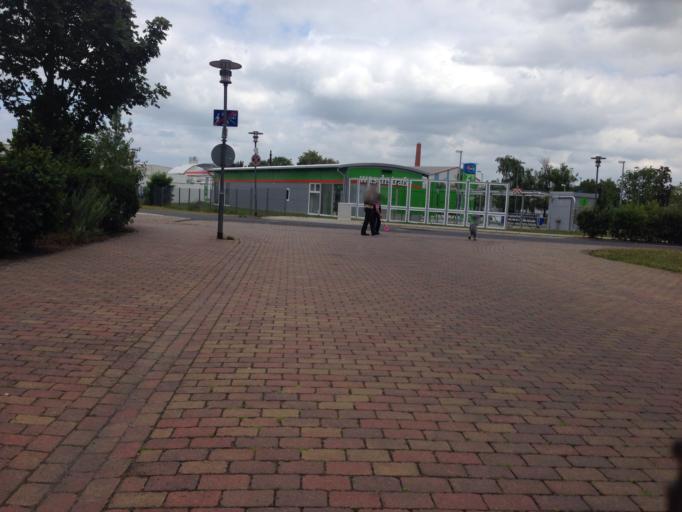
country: DE
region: Hesse
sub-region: Regierungsbezirk Darmstadt
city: Hanau am Main
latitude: 50.1442
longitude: 8.9365
